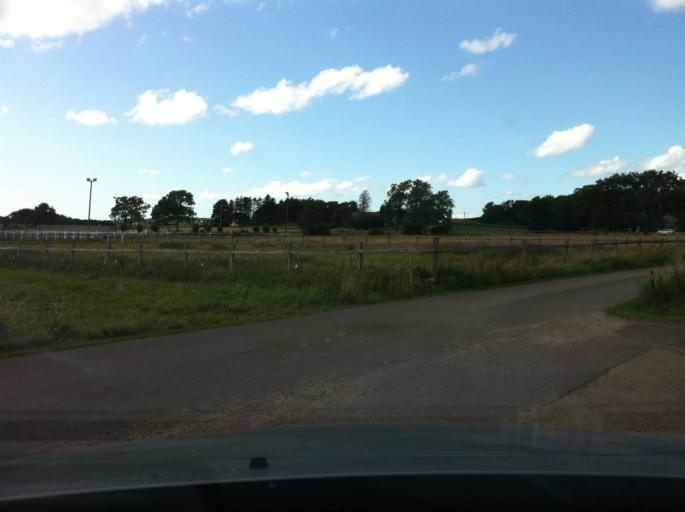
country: SE
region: Skane
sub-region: Bastads Kommun
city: Bastad
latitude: 56.4327
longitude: 12.7622
